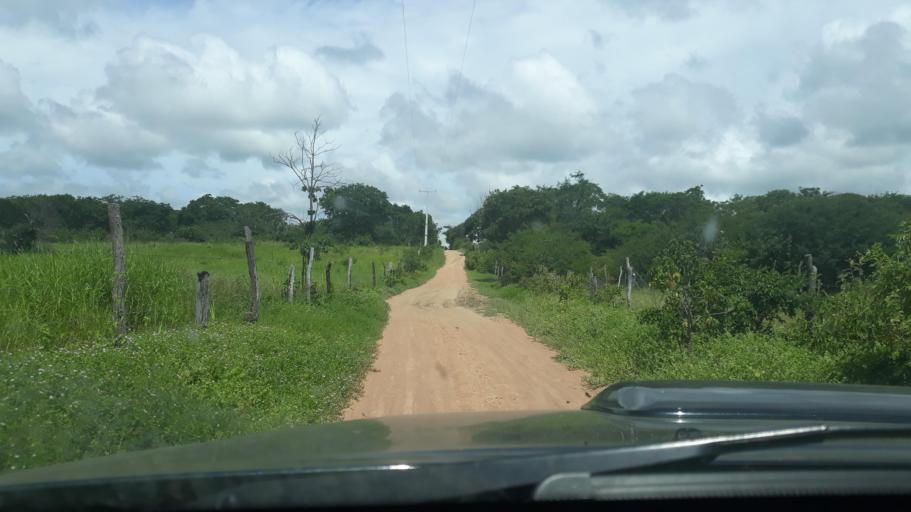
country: BR
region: Bahia
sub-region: Riacho De Santana
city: Riacho de Santana
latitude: -13.8645
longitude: -43.0178
